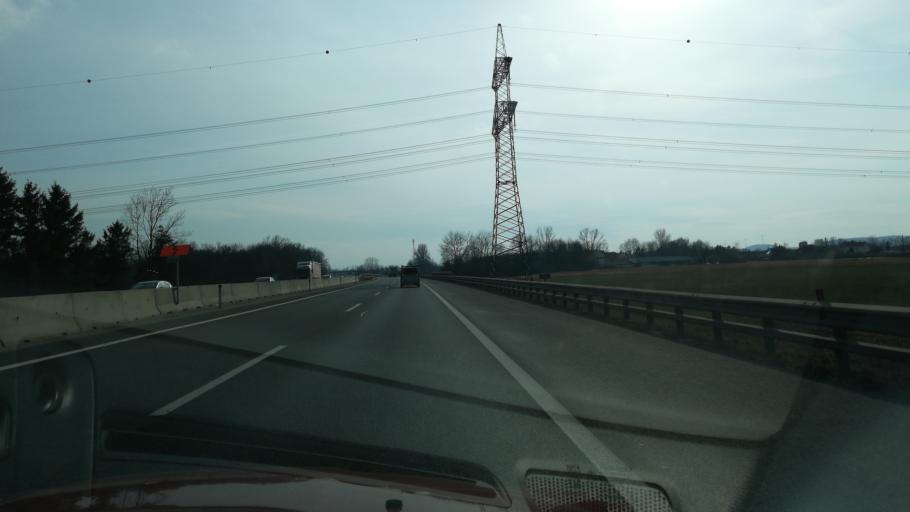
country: AT
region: Lower Austria
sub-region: Politischer Bezirk Sankt Polten
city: Traismauer
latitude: 48.3292
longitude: 15.7205
